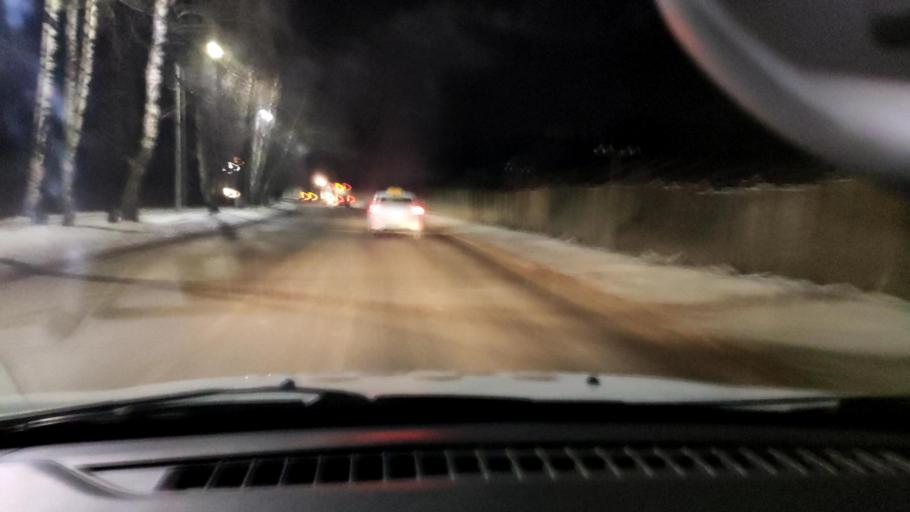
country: RU
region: Perm
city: Kultayevo
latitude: 57.9874
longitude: 55.9242
